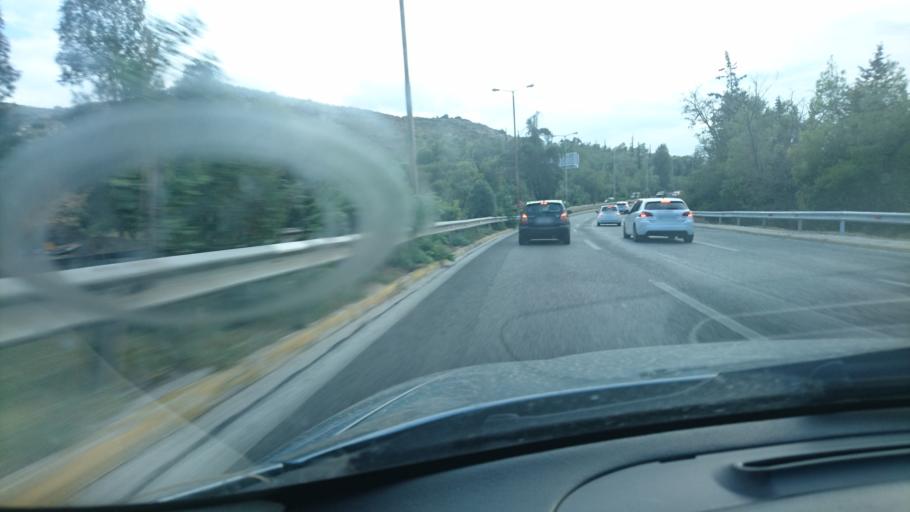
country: GR
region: Attica
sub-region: Nomarchia Athinas
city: Kaisariani
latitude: 37.9622
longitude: 23.7789
